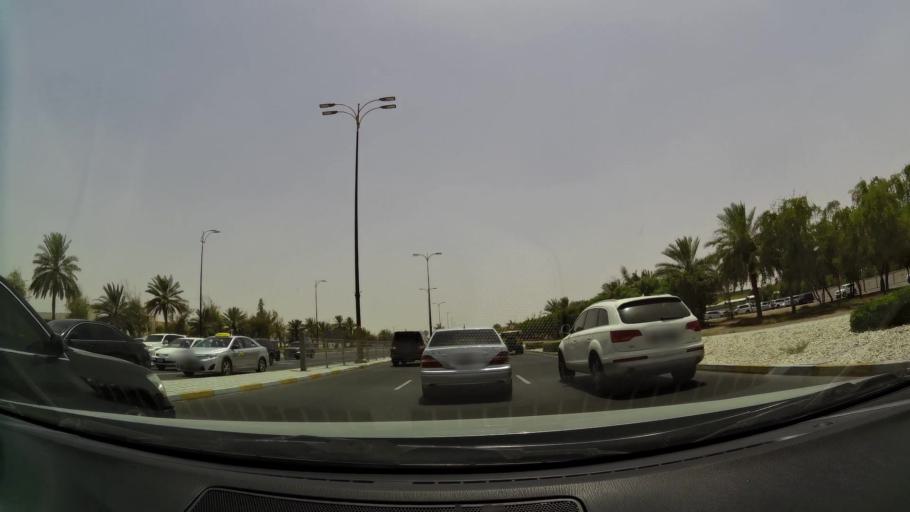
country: AE
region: Abu Dhabi
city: Al Ain
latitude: 24.2005
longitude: 55.7147
